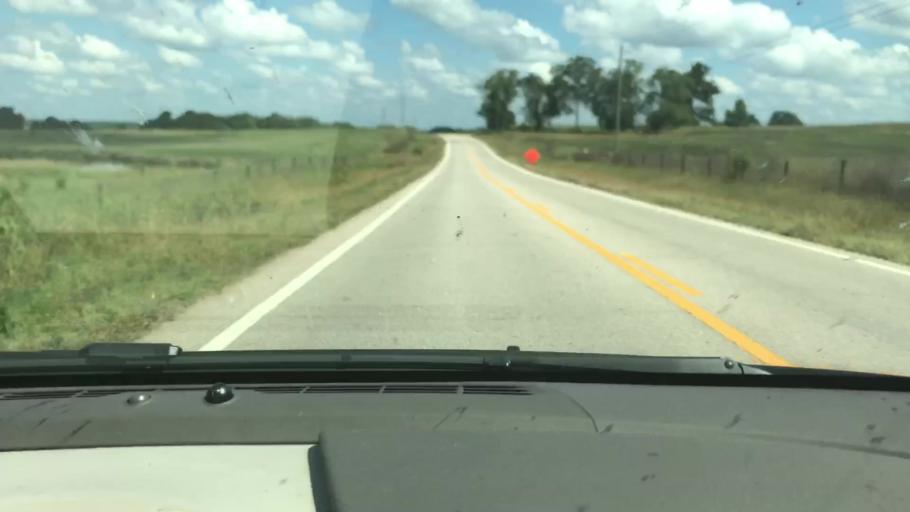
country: US
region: Georgia
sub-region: Troup County
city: West Point
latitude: 32.8805
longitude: -85.0337
